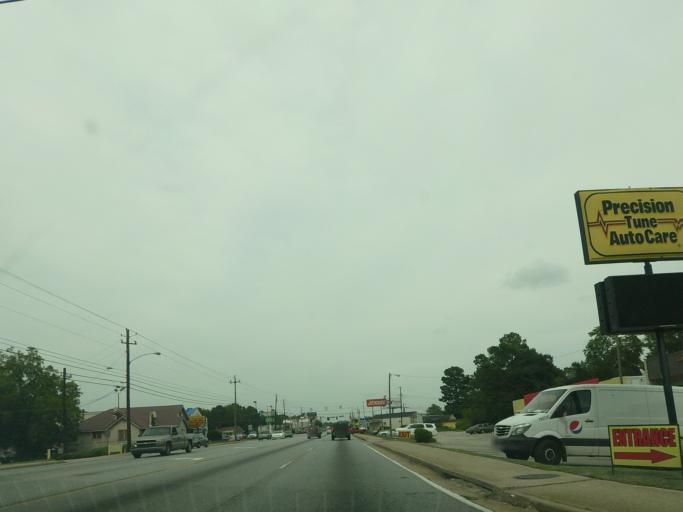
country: US
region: Georgia
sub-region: Bibb County
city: Macon
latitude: 32.8229
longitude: -83.6833
